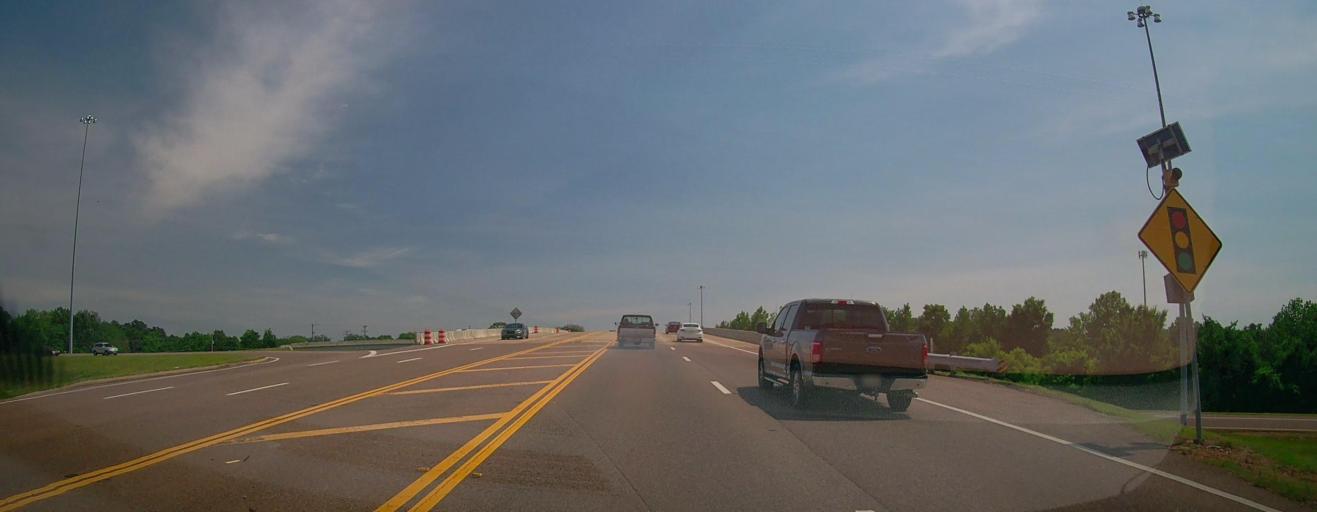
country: US
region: Mississippi
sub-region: De Soto County
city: Olive Branch
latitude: 34.9683
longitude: -89.8305
